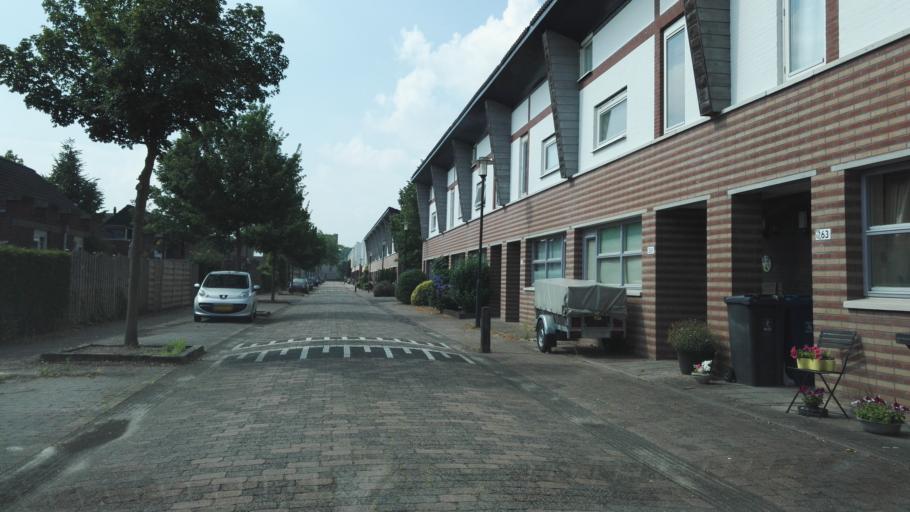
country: NL
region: Gelderland
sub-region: Gemeente Apeldoorn
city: Apeldoorn
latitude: 52.2138
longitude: 6.0139
